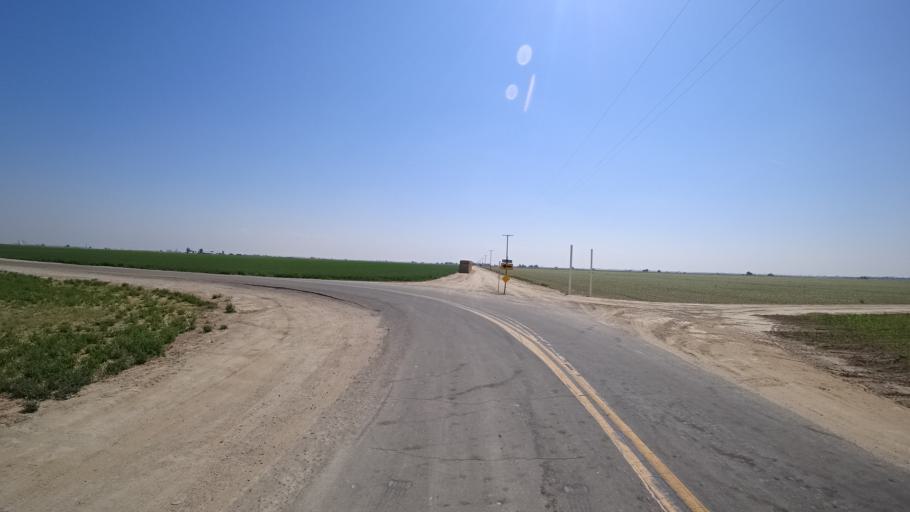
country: US
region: California
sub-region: Tulare County
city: Goshen
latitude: 36.3722
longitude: -119.5292
